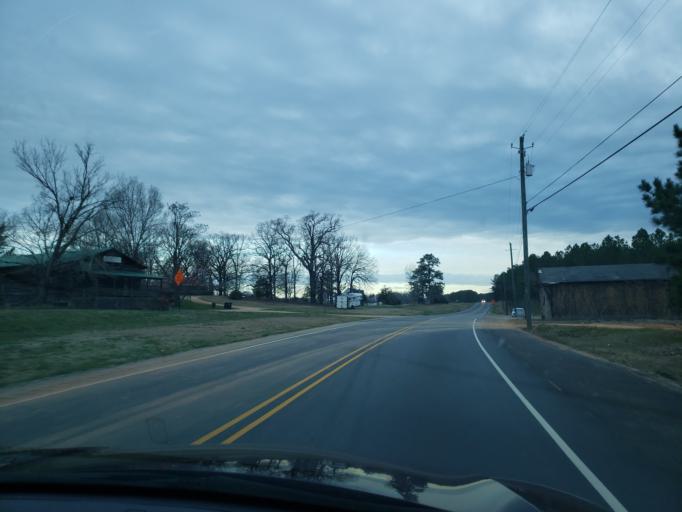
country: US
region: Alabama
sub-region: Randolph County
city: Roanoke
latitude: 33.0573
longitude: -85.3315
